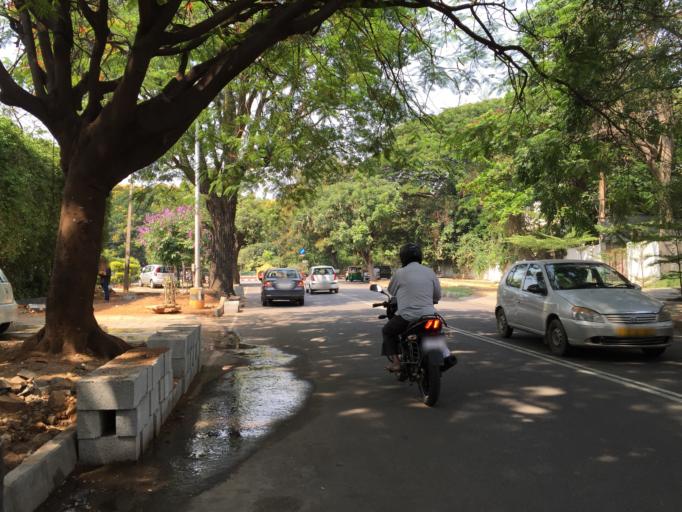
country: IN
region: Karnataka
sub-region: Bangalore Urban
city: Bangalore
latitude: 12.9450
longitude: 77.5779
